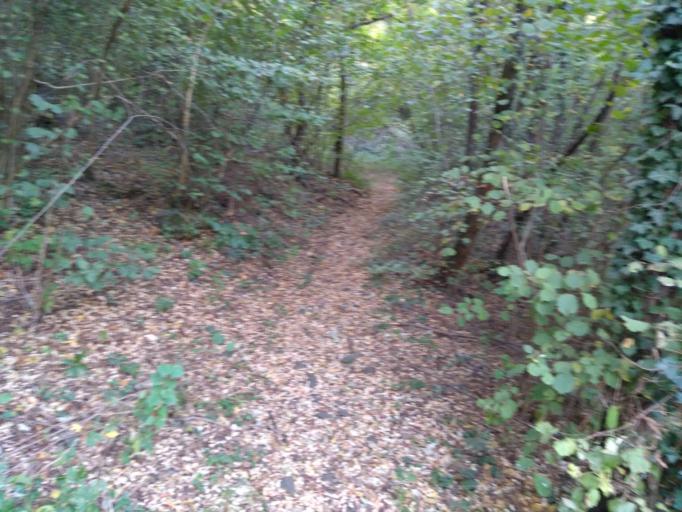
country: IT
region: Veneto
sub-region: Provincia di Vicenza
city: Malo
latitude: 45.6484
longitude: 11.4047
